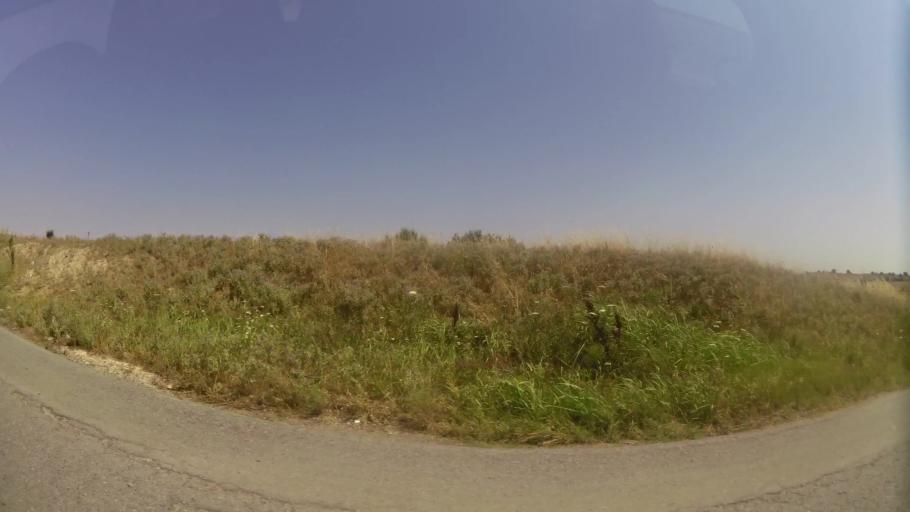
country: GR
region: Central Macedonia
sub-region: Nomos Thessalonikis
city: Neoi Epivates
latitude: 40.4662
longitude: 22.9018
